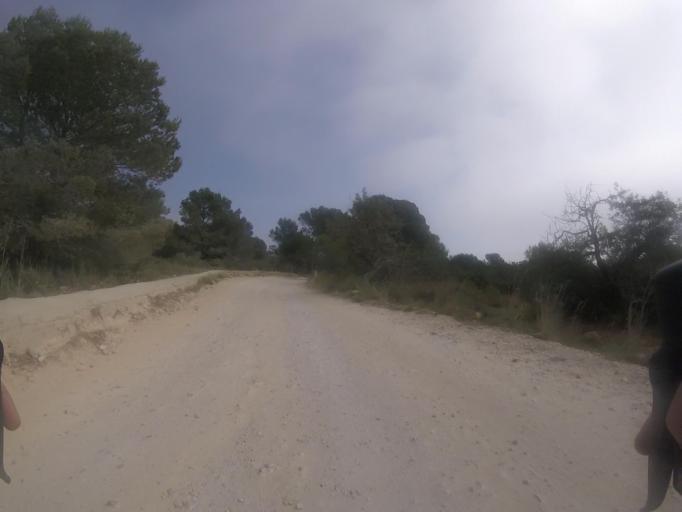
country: ES
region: Valencia
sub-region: Provincia de Castello
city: Alcoceber
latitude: 40.2601
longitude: 0.2970
